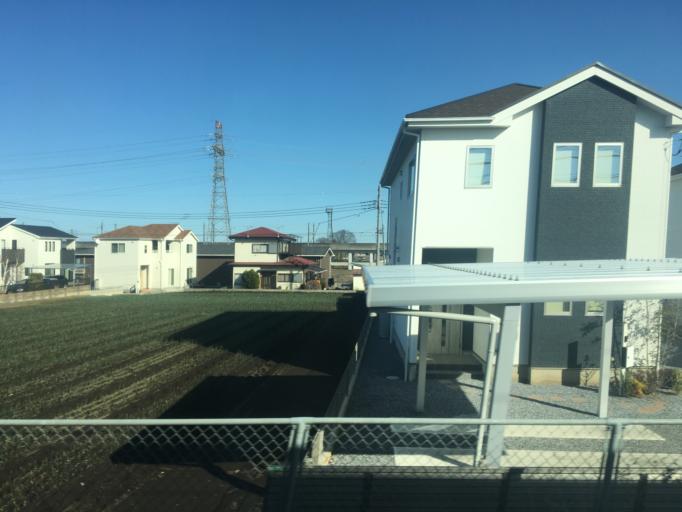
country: JP
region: Tochigi
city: Utsunomiya-shi
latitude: 36.5030
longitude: 139.8787
